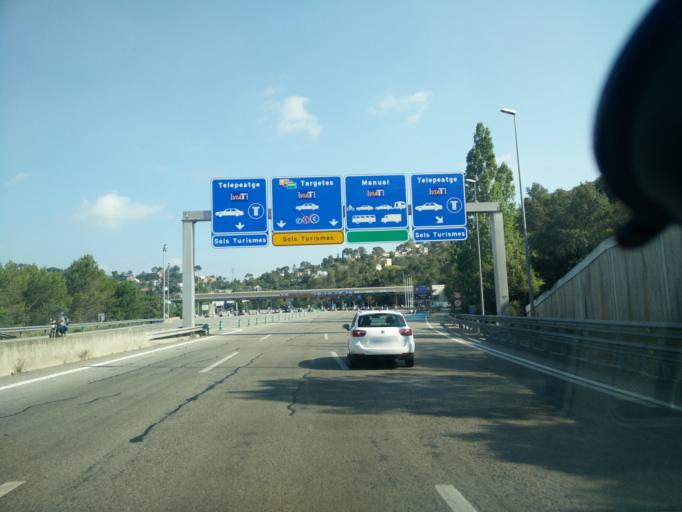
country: ES
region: Catalonia
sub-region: Provincia de Barcelona
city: Sant Cugat del Valles
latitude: 41.4354
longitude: 2.0759
